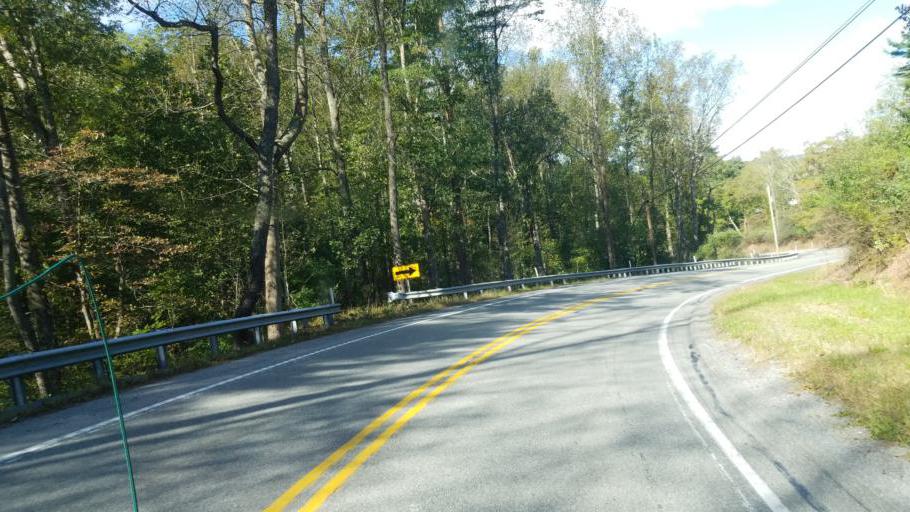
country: US
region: Pennsylvania
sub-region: Fulton County
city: McConnellsburg
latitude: 39.9757
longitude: -78.0387
